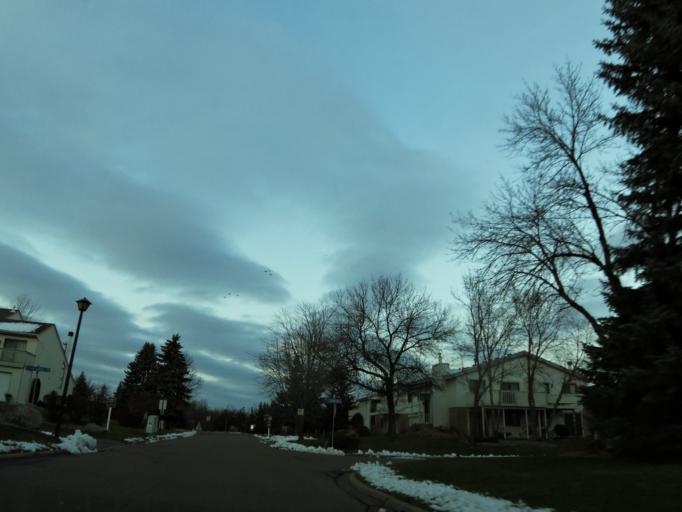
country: US
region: Minnesota
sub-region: Hennepin County
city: Minnetonka Mills
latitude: 44.9054
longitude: -93.4251
